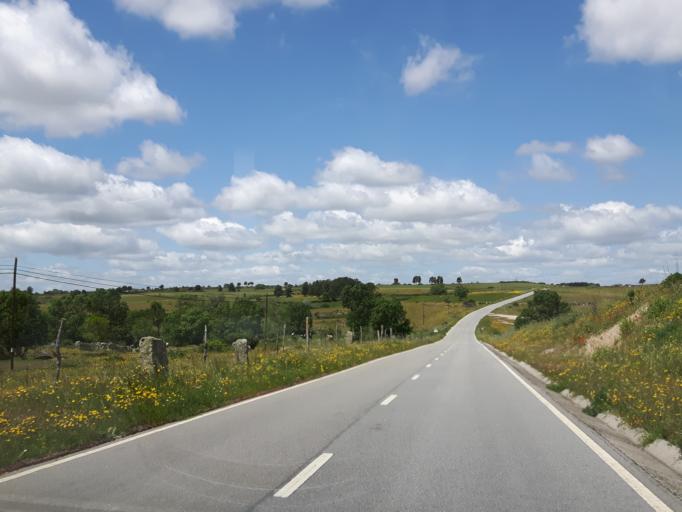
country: ES
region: Castille and Leon
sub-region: Provincia de Salamanca
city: Aldea del Obispo
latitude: 40.7106
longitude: -6.8505
